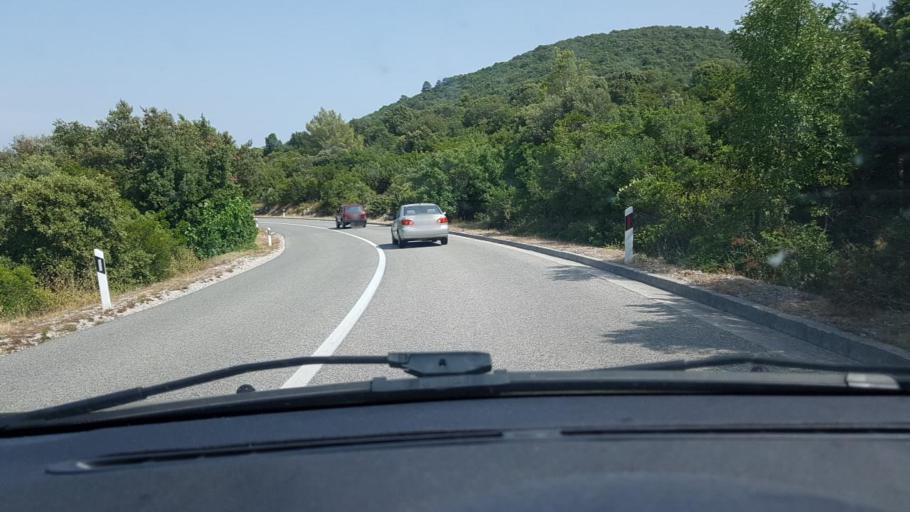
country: HR
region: Dubrovacko-Neretvanska
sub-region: Grad Korcula
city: Zrnovo
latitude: 42.9411
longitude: 17.0554
